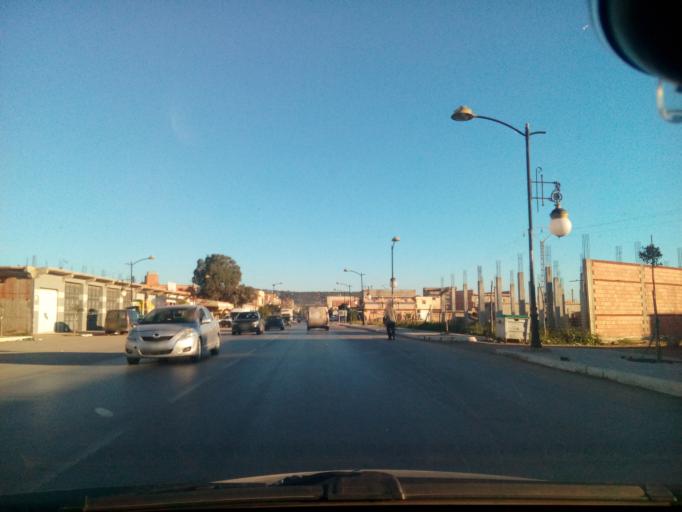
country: DZ
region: Mostaganem
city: Mostaganem
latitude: 35.7832
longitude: 0.1826
